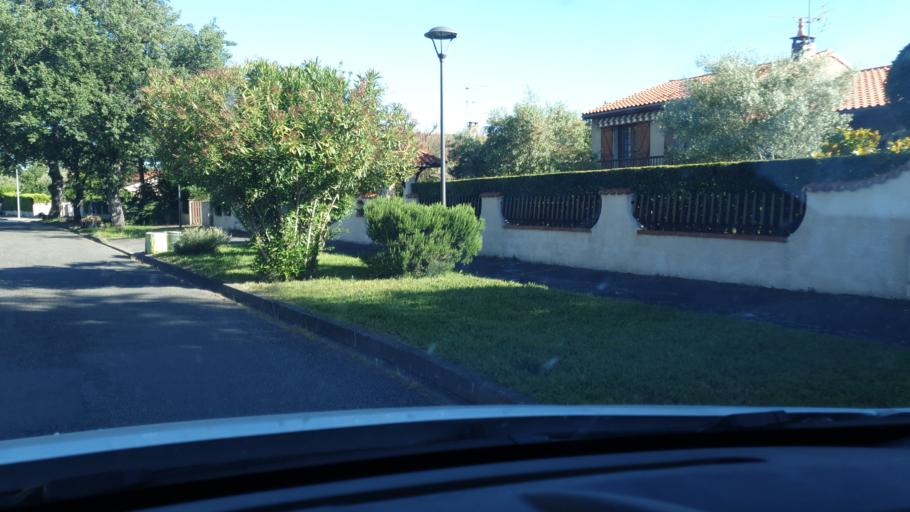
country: FR
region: Midi-Pyrenees
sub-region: Departement de la Haute-Garonne
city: Saint-Orens-de-Gameville
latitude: 43.5578
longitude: 1.5174
